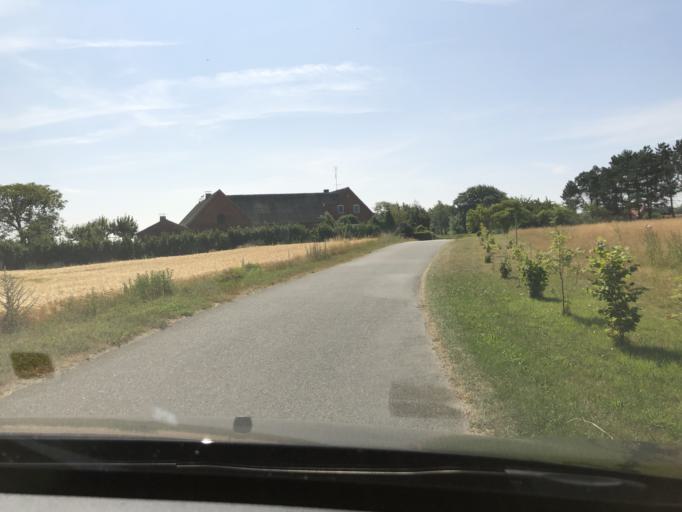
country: DK
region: South Denmark
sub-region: AEro Kommune
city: AEroskobing
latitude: 54.9218
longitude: 10.2976
